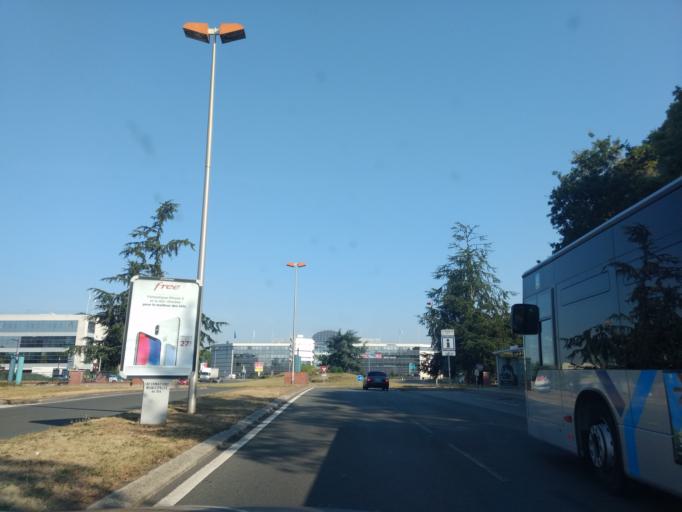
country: FR
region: Ile-de-France
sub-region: Departement des Yvelines
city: Saint-Cyr-l'Ecole
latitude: 48.7846
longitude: 2.0604
